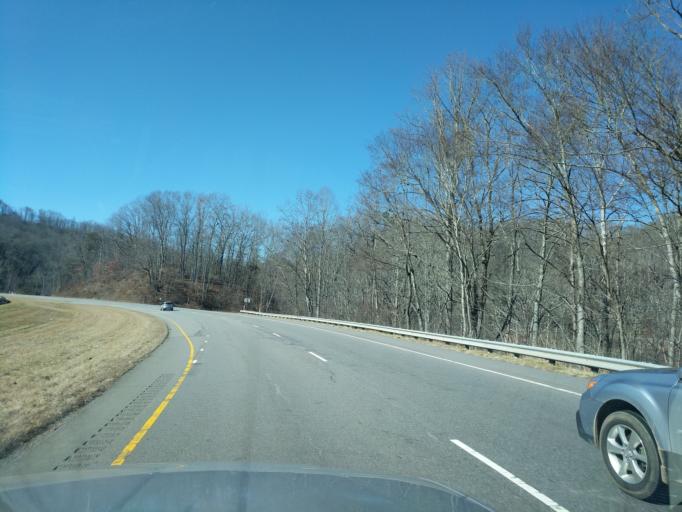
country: US
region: North Carolina
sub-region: Jackson County
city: Cullowhee
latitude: 35.3981
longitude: -83.1322
